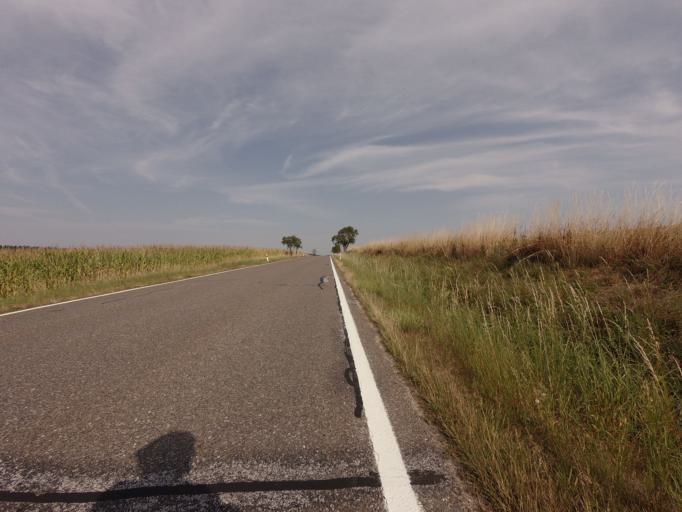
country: CZ
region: Central Bohemia
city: Petrovice
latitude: 49.5105
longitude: 14.3617
